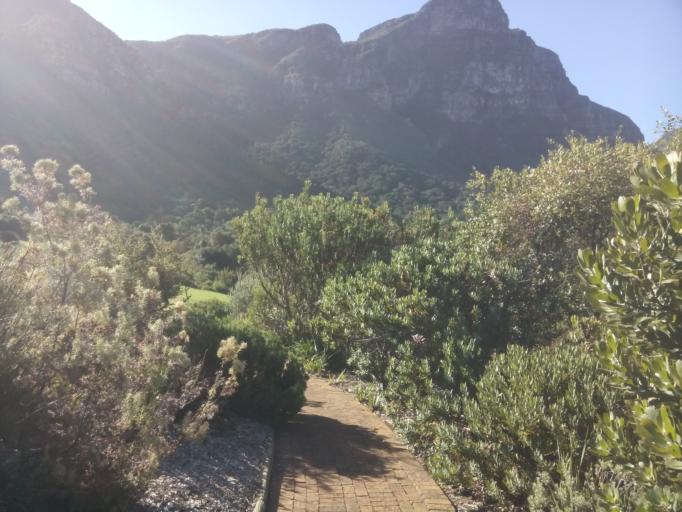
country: ZA
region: Western Cape
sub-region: City of Cape Town
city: Newlands
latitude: -33.9903
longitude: 18.4288
